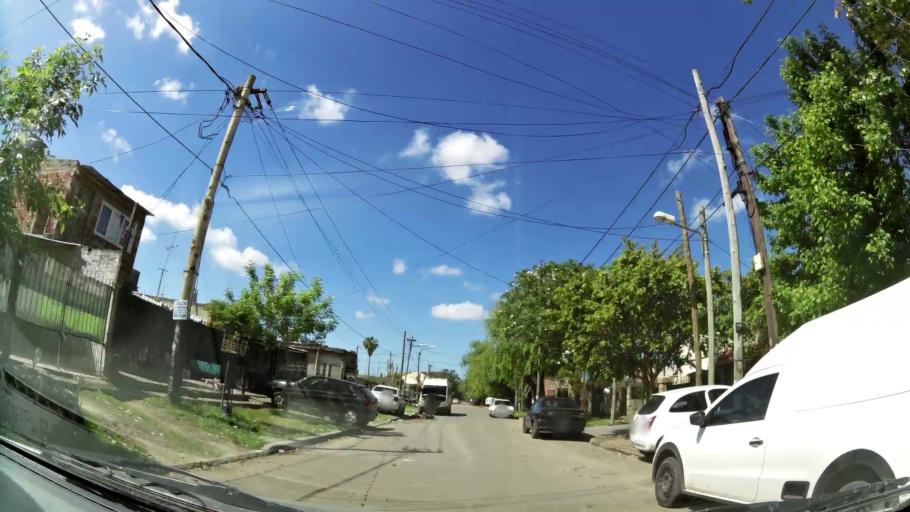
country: AR
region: Buenos Aires
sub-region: Partido de Quilmes
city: Quilmes
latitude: -34.8239
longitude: -58.2740
